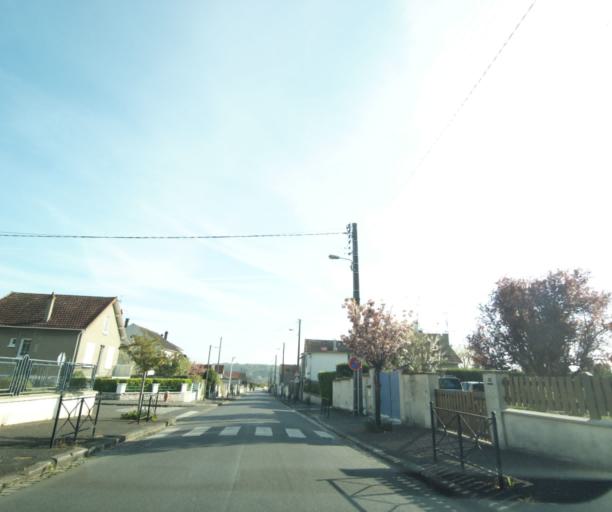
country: FR
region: Ile-de-France
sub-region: Departement de Seine-et-Marne
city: Moret-sur-Loing
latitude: 48.3679
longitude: 2.8128
